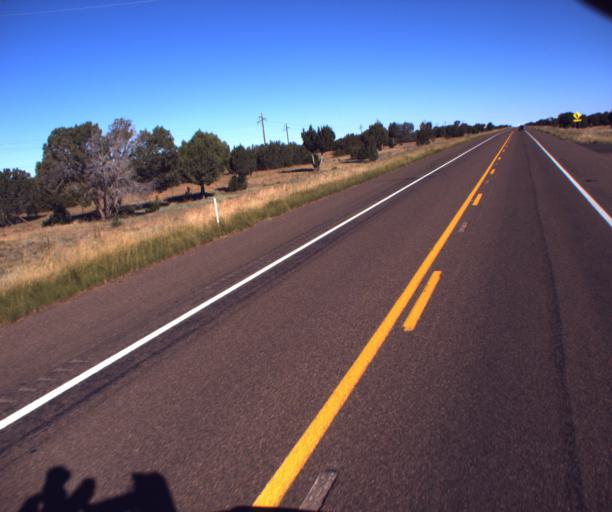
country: US
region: Arizona
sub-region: Navajo County
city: Show Low
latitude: 34.2738
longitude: -110.0245
